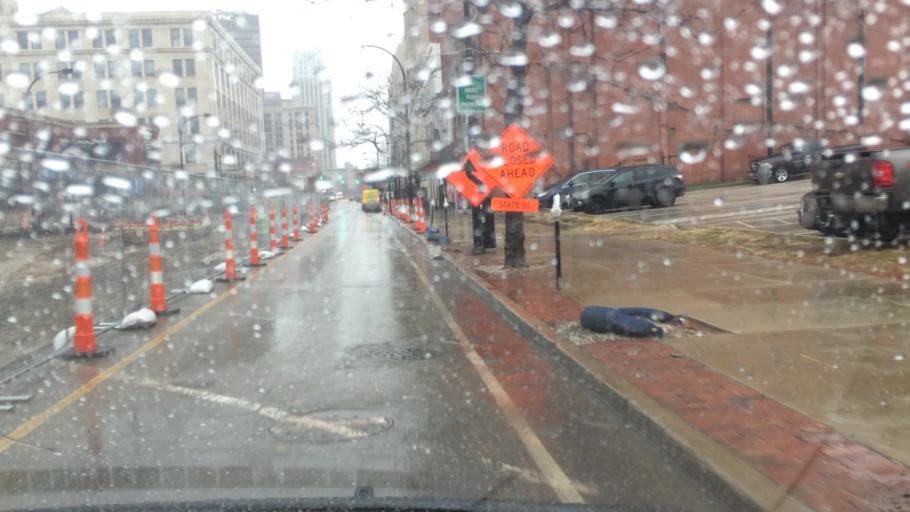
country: US
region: Ohio
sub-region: Summit County
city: Akron
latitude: 41.0773
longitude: -81.5214
